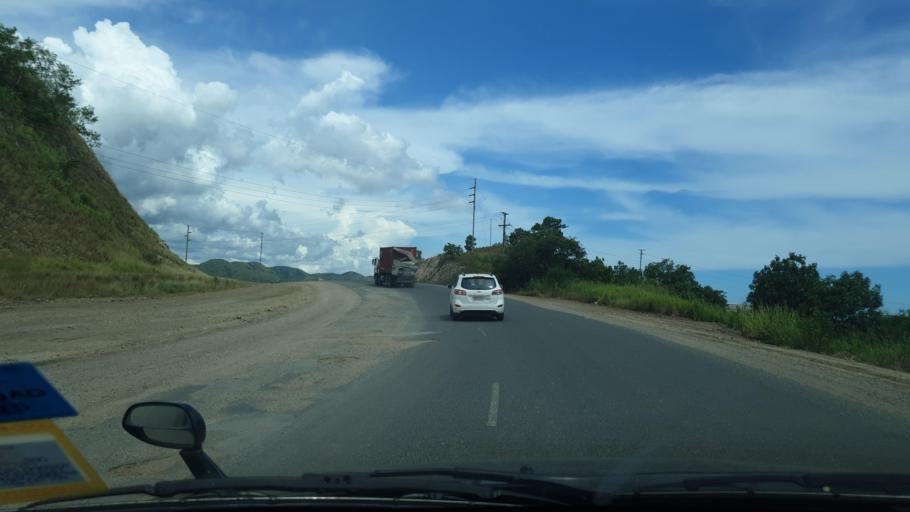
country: PG
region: National Capital
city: Port Moresby
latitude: -9.4177
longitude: 147.1033
